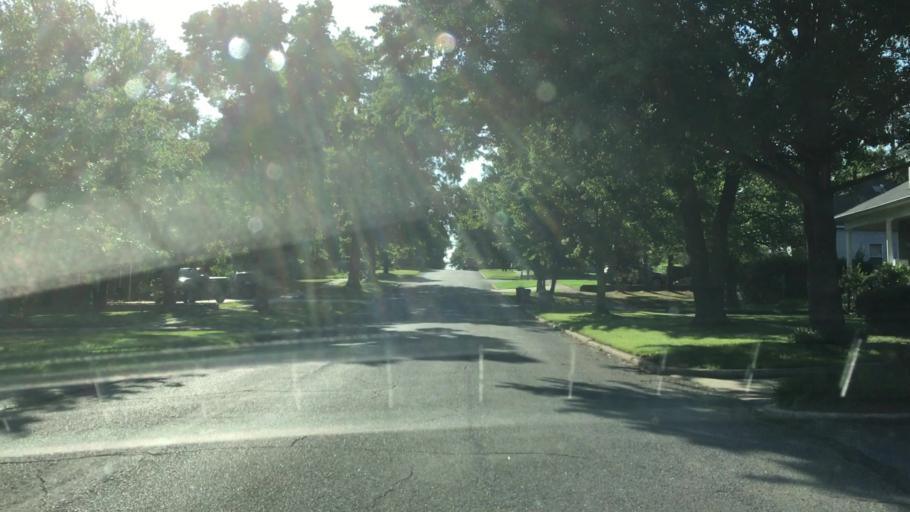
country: US
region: Oklahoma
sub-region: Cherokee County
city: Tahlequah
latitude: 35.9132
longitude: -94.9746
